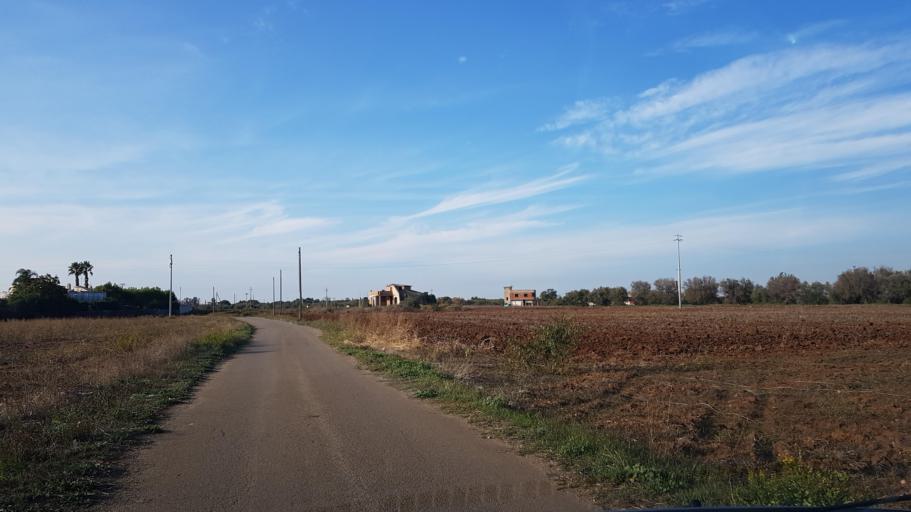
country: IT
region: Apulia
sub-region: Provincia di Brindisi
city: Mesagne
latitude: 40.5394
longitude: 17.8265
